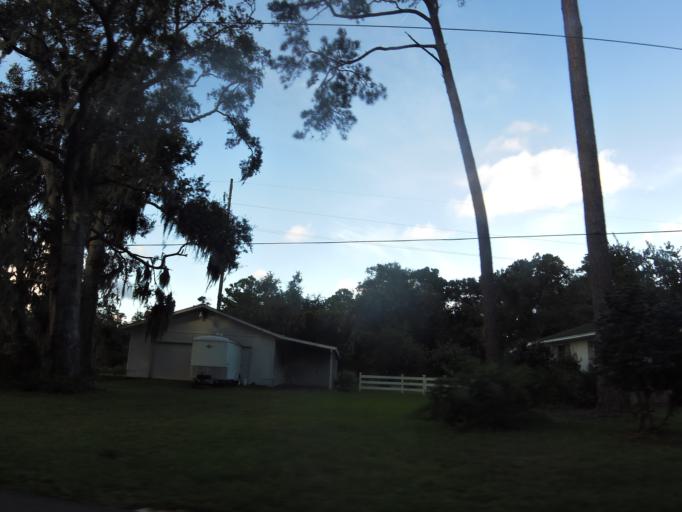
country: US
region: Georgia
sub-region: Camden County
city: St. Marys
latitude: 30.7396
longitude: -81.5608
